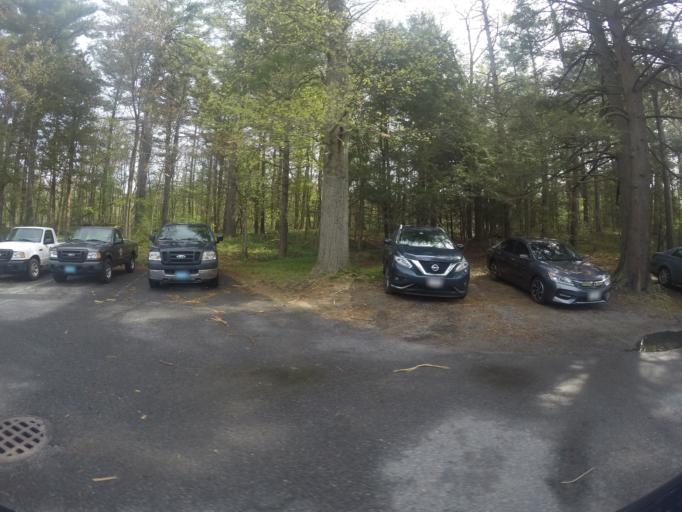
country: US
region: Massachusetts
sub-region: Norfolk County
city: Stoughton
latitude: 42.0751
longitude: -71.0948
